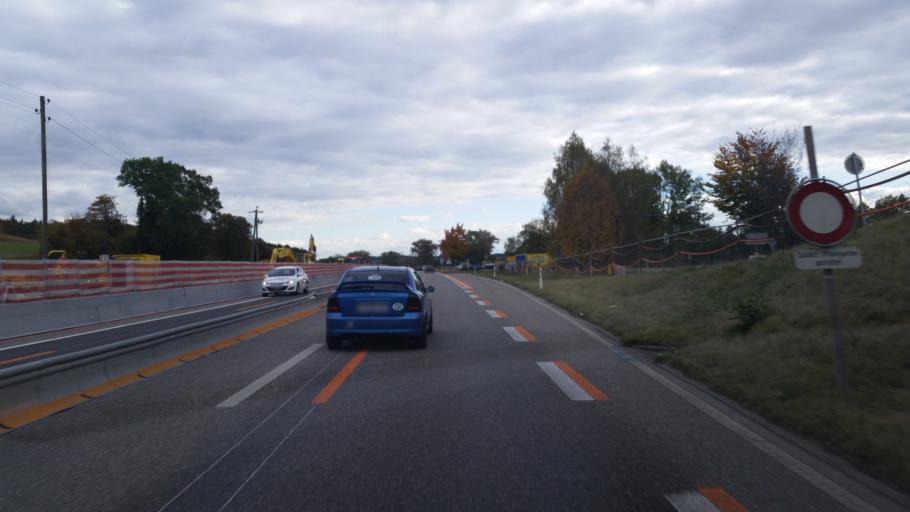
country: CH
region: Zurich
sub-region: Bezirk Buelach
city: Kloten / Freienberg (Chanzler-Chlini Chaseren)
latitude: 47.4749
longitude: 8.5546
